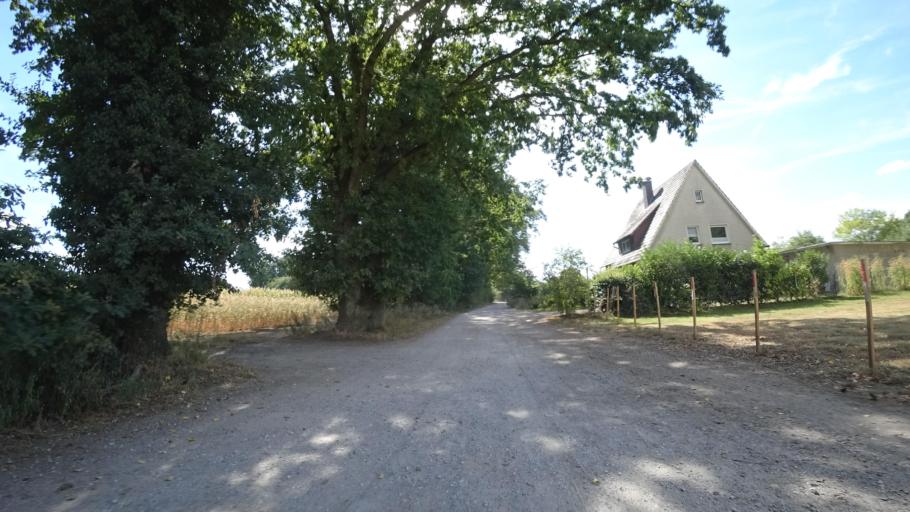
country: DE
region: North Rhine-Westphalia
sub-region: Regierungsbezirk Detmold
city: Verl
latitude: 51.9412
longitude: 8.4947
